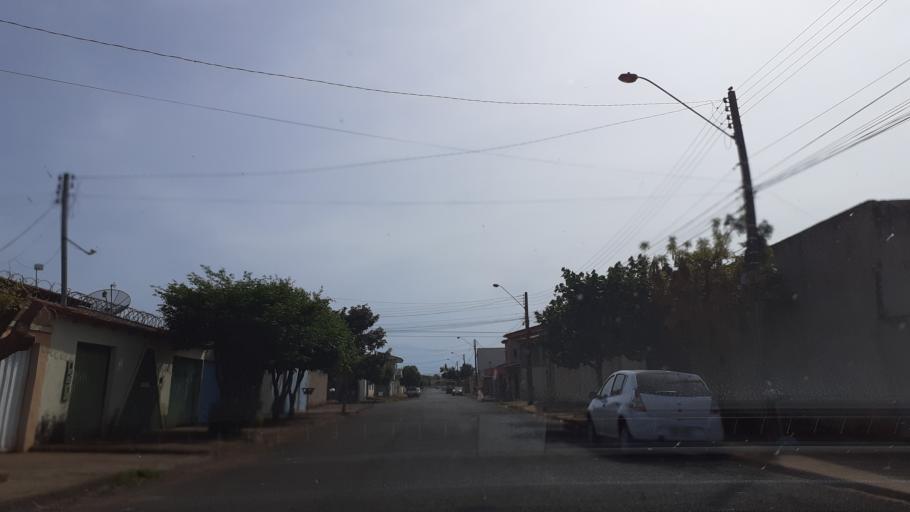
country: BR
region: Goias
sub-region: Itumbiara
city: Itumbiara
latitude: -18.4235
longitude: -49.2412
